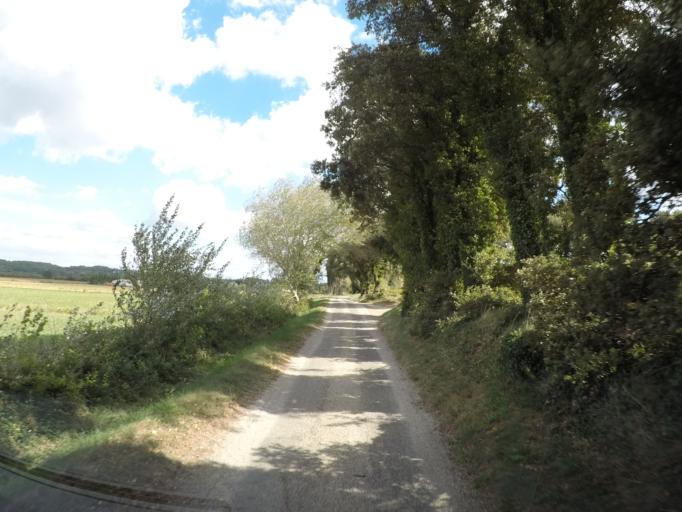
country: FR
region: Rhone-Alpes
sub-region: Departement de la Drome
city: Saint-Restitut
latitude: 44.3005
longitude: 4.8022
